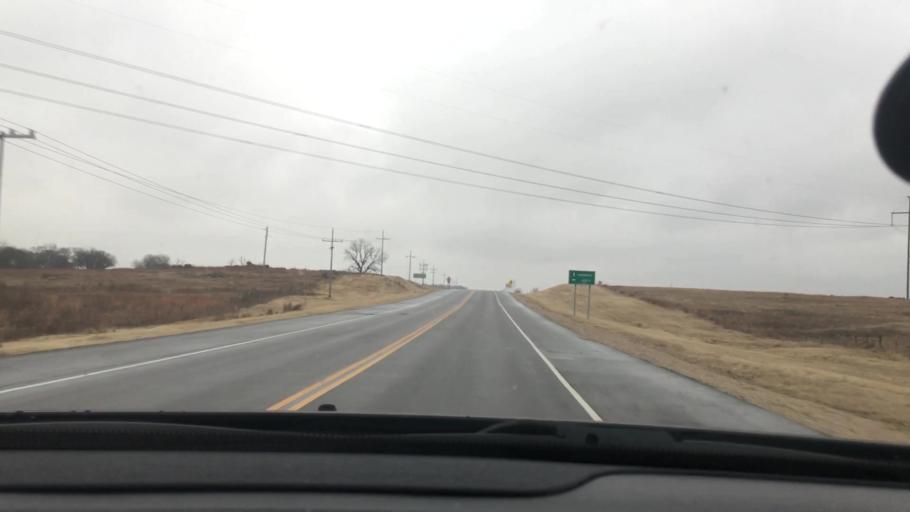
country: US
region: Oklahoma
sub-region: Johnston County
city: Tishomingo
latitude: 34.3674
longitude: -96.6360
